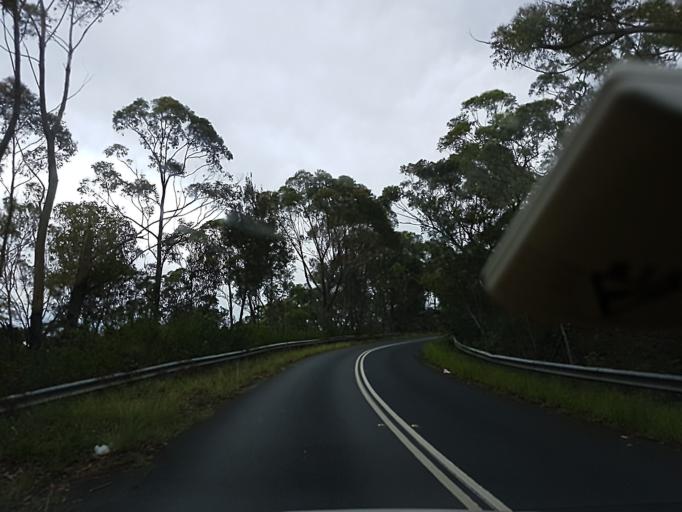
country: AU
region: New South Wales
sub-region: Warringah
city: Davidson
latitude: -33.7282
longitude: 151.2329
